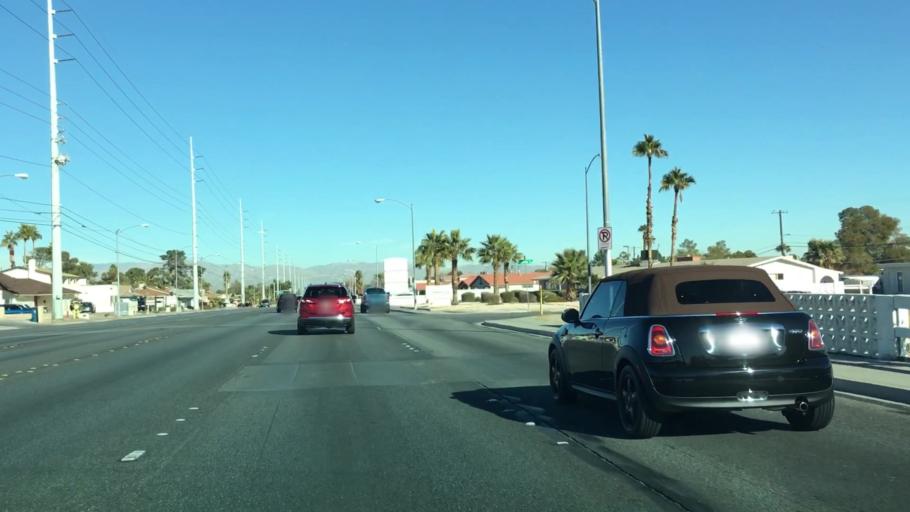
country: US
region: Nevada
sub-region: Clark County
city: Paradise
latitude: 36.0896
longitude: -115.1188
